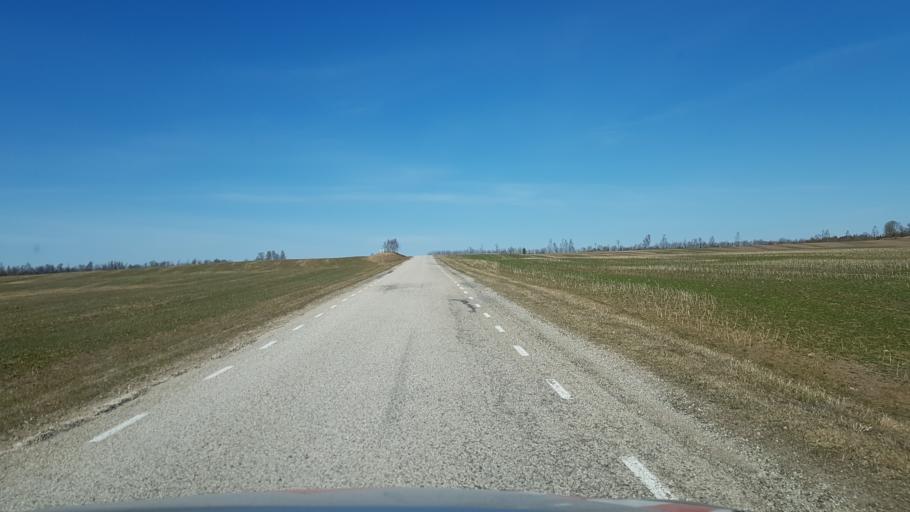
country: EE
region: Laeaene-Virumaa
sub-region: Vinni vald
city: Vinni
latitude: 59.0734
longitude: 26.5531
